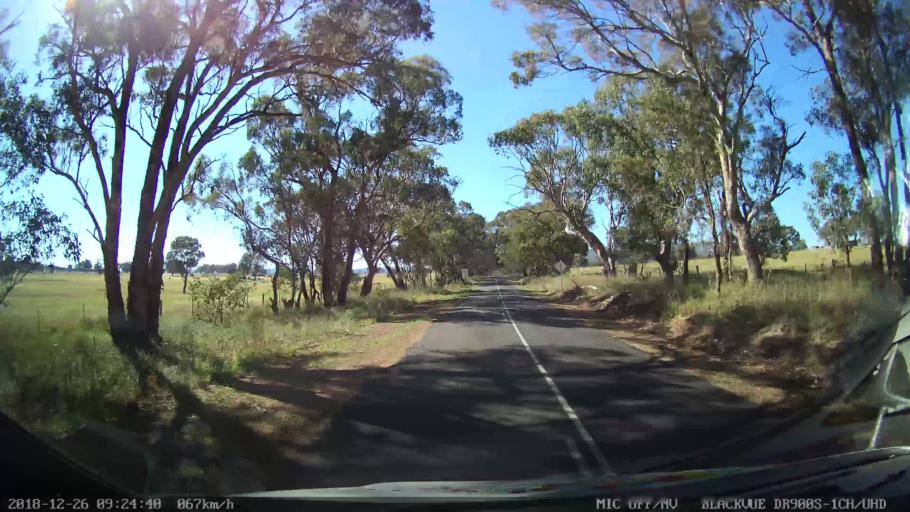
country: AU
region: New South Wales
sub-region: Mid-Western Regional
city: Kandos
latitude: -32.8124
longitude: 150.0004
